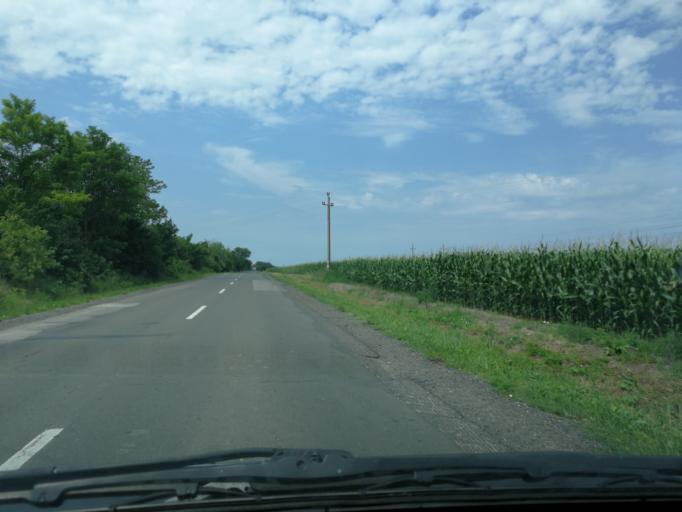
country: HU
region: Baranya
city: Siklos
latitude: 45.8498
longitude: 18.3492
